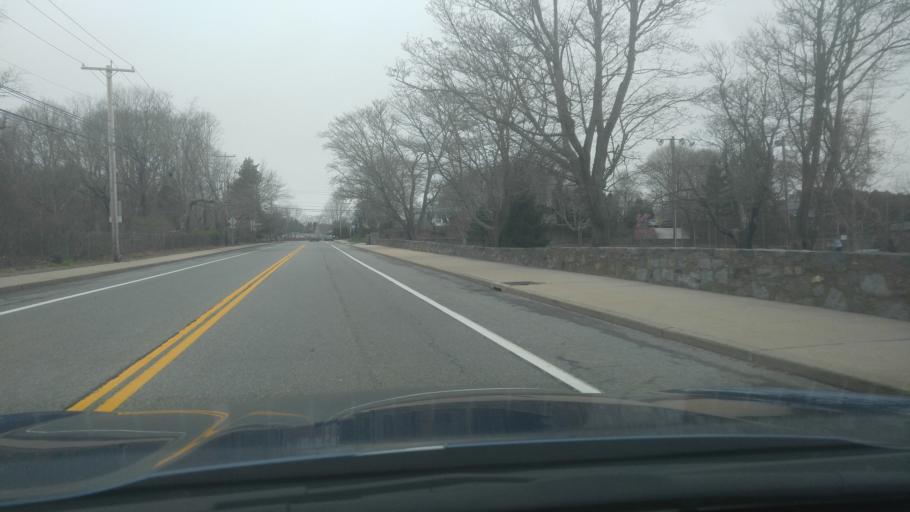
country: US
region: Rhode Island
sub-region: Washington County
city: Narragansett Pier
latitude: 41.4344
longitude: -71.4707
